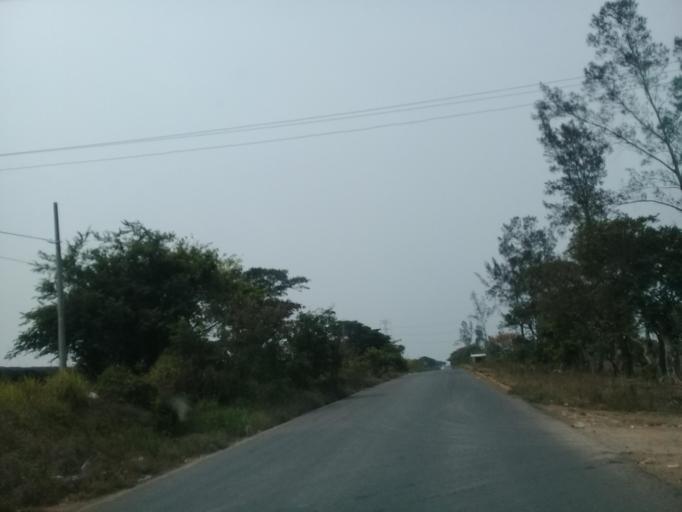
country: MX
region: Veracruz
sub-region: Medellin
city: La Laguna y Monte del Castillo
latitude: 18.9861
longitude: -96.1171
